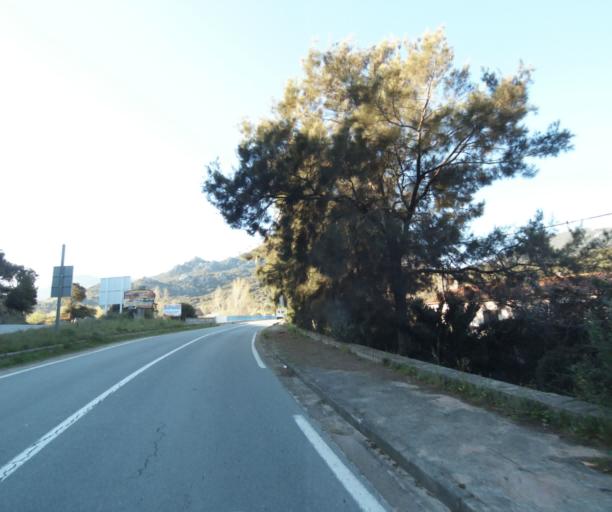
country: FR
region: Corsica
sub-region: Departement de la Corse-du-Sud
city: Propriano
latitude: 41.6583
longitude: 8.9175
